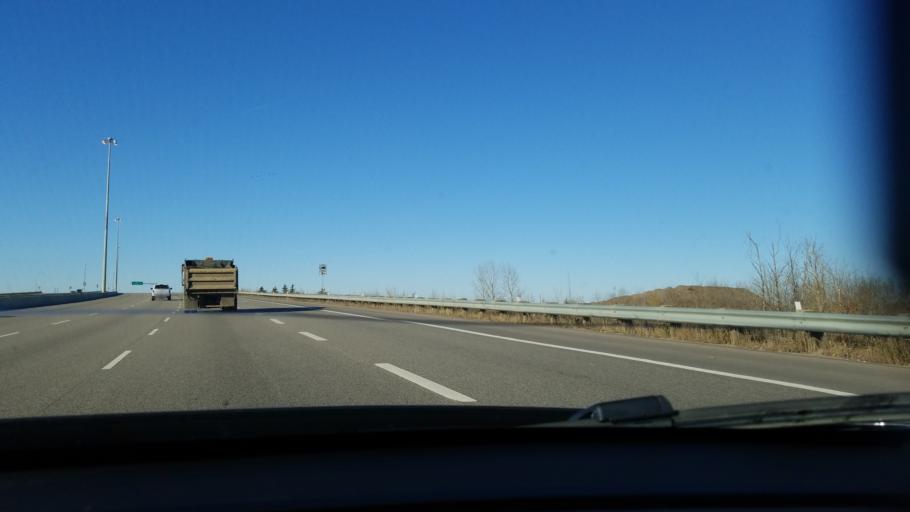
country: CA
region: Alberta
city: Sherwood Park
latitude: 53.4830
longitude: -113.3584
